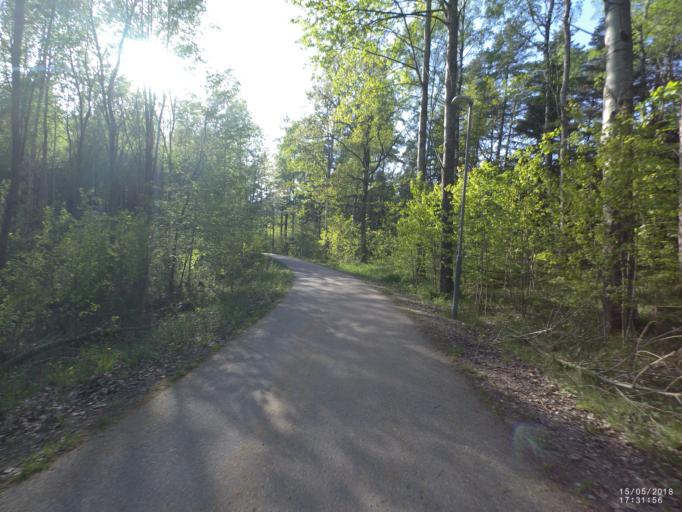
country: SE
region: Soedermanland
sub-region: Nykopings Kommun
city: Nykoping
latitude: 58.7350
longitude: 17.0155
